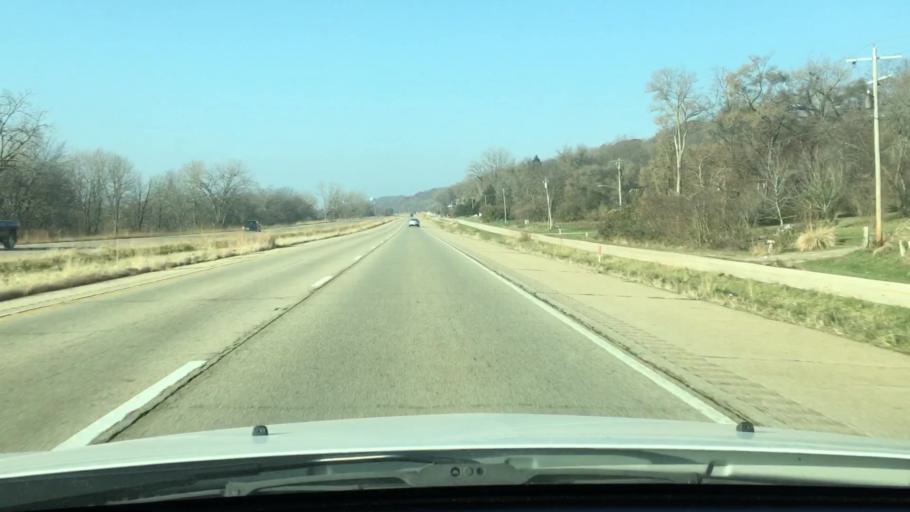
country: US
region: Illinois
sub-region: Peoria County
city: Glasford
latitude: 40.5603
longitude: -89.7593
